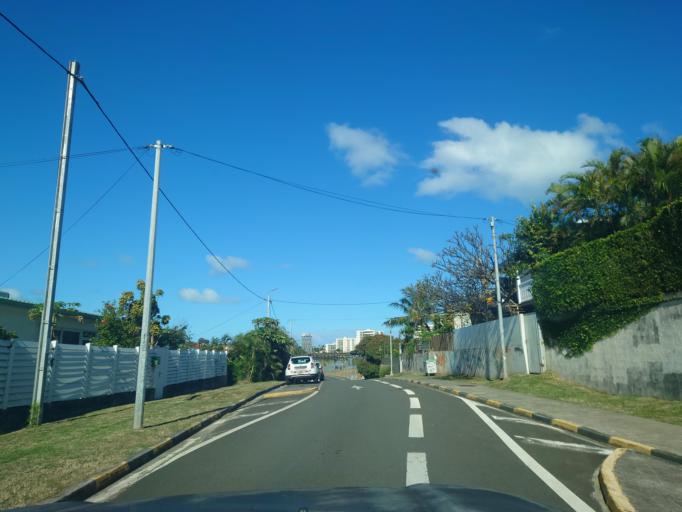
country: NC
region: South Province
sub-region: Noumea
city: Noumea
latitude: -22.2674
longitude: 166.4700
